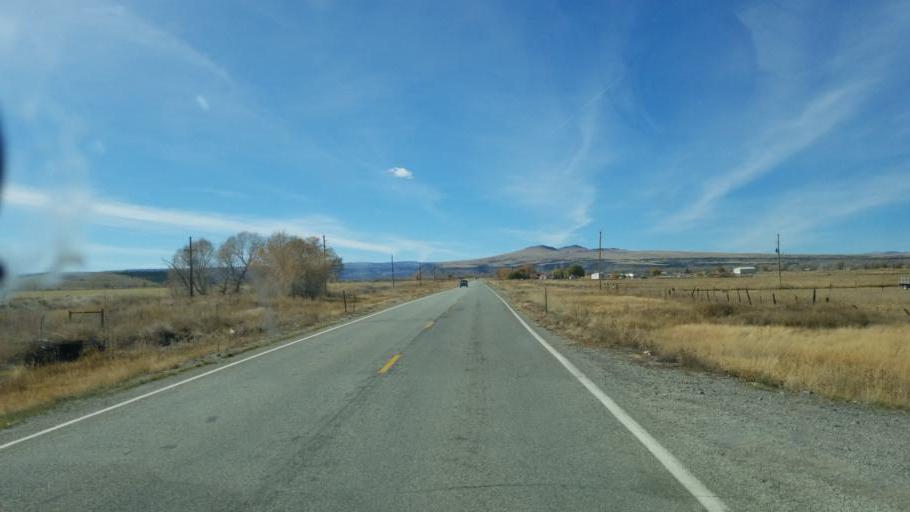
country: US
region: Colorado
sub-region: Conejos County
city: Conejos
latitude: 37.0645
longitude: -106.0464
